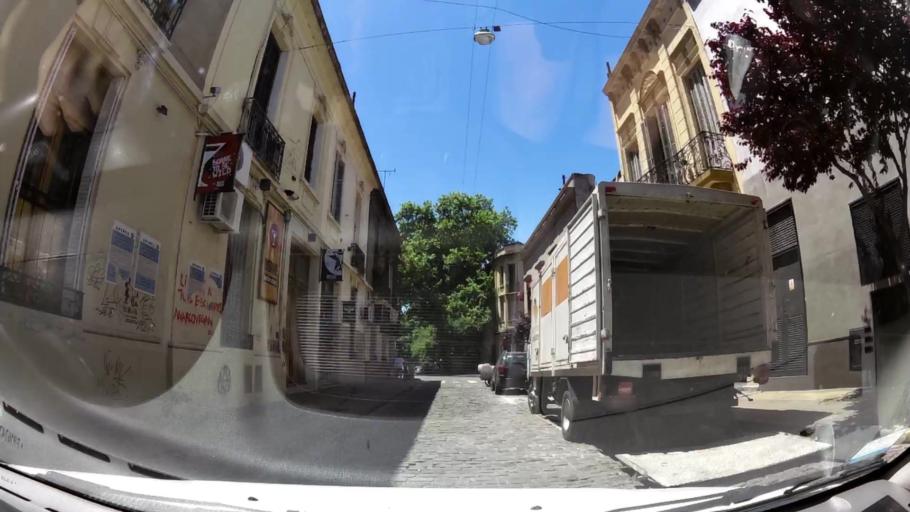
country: AR
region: Buenos Aires F.D.
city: Buenos Aires
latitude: -34.6160
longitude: -58.3722
